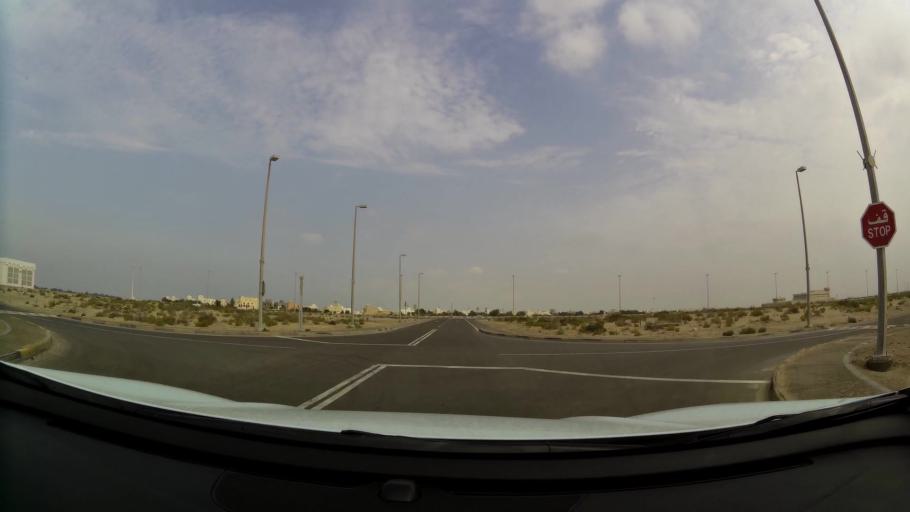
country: AE
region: Abu Dhabi
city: Abu Dhabi
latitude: 24.6369
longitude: 54.6714
